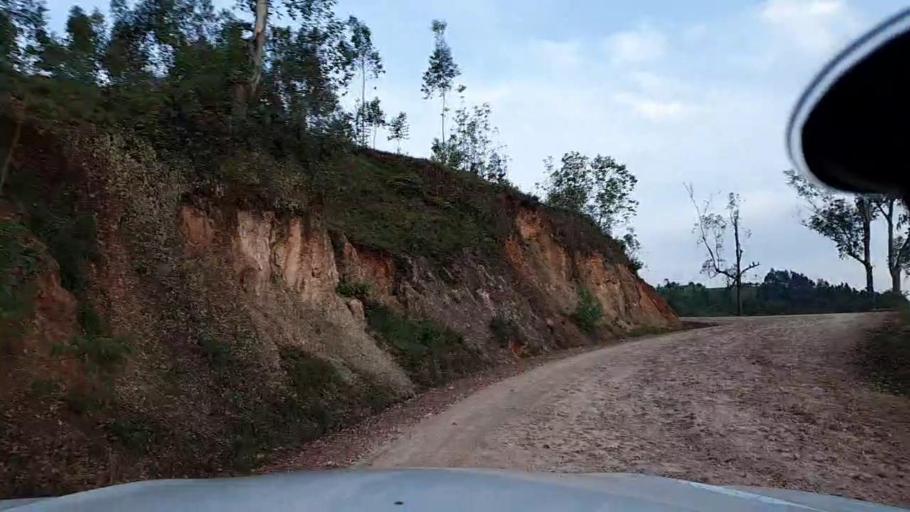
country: RW
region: Southern Province
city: Nyanza
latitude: -2.2120
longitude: 29.6308
